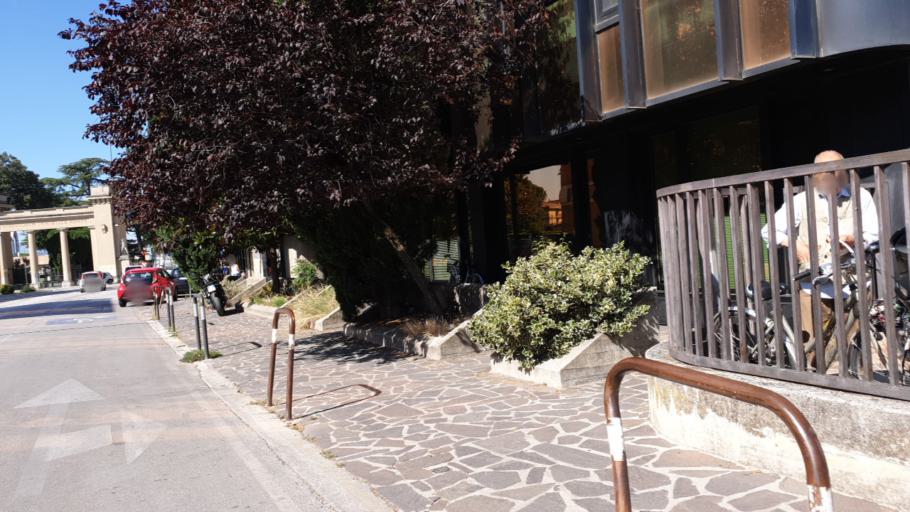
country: IT
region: Umbria
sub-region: Provincia di Perugia
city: Foligno
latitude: 42.9538
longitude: 12.7073
